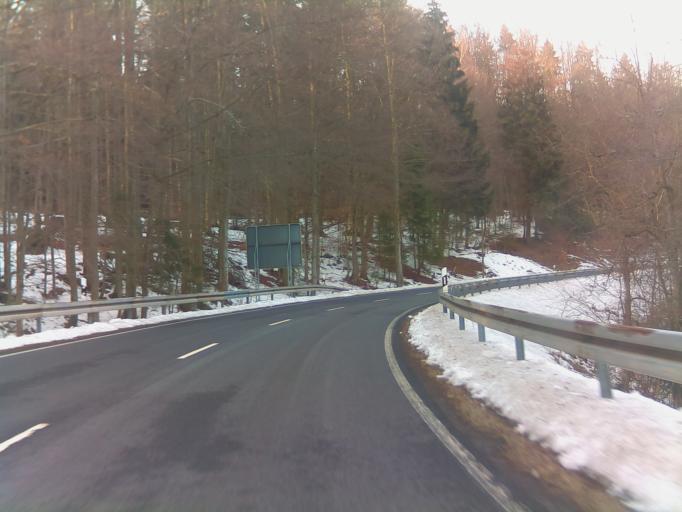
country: DE
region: Bavaria
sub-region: Regierungsbezirk Unterfranken
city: Wildflecken
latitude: 50.3654
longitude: 9.9201
